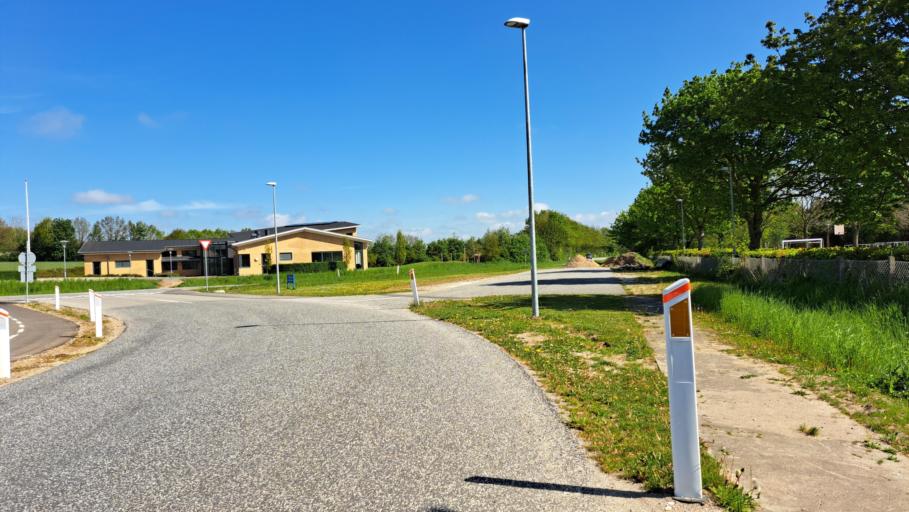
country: DK
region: Central Jutland
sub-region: Hedensted Kommune
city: Hedensted
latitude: 55.7981
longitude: 9.6520
